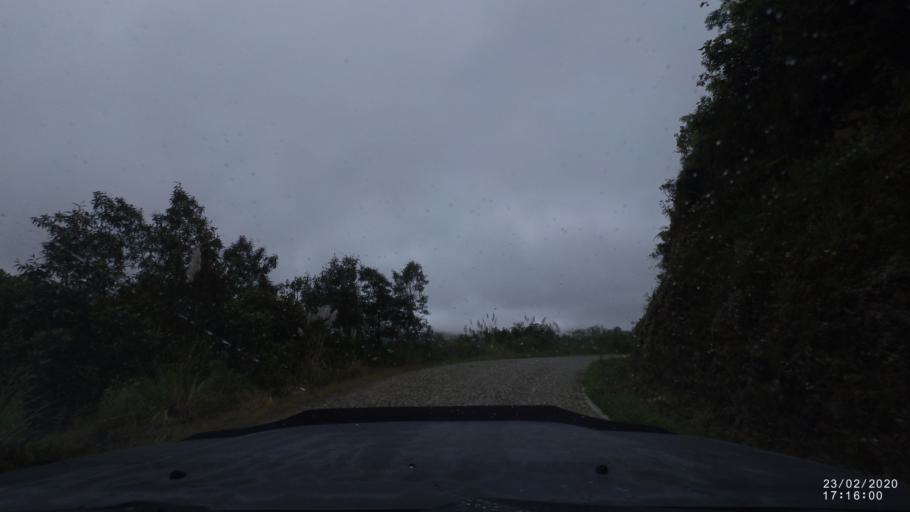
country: BO
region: Cochabamba
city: Colomi
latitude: -17.1342
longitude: -65.9395
